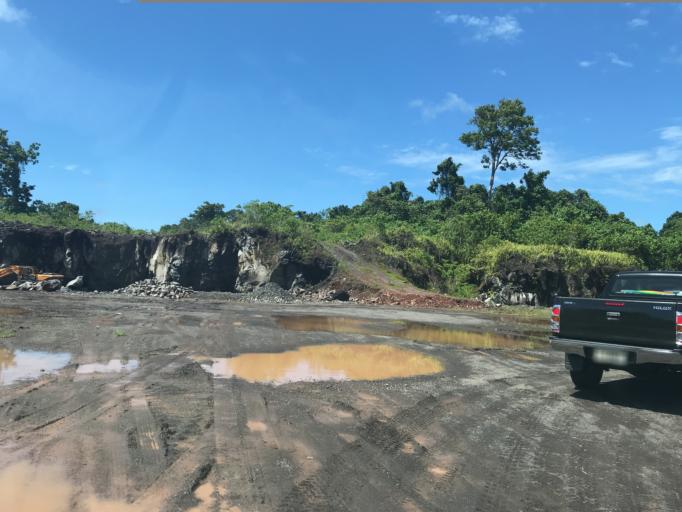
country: WS
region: Palauli
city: Vailoa
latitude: -13.7465
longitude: -172.2716
